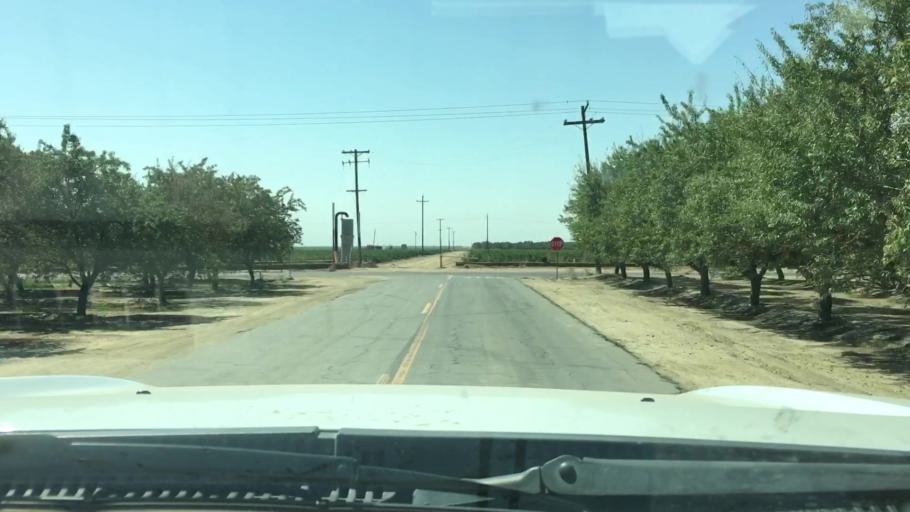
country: US
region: California
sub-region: Kern County
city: Shafter
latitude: 35.4781
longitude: -119.3136
